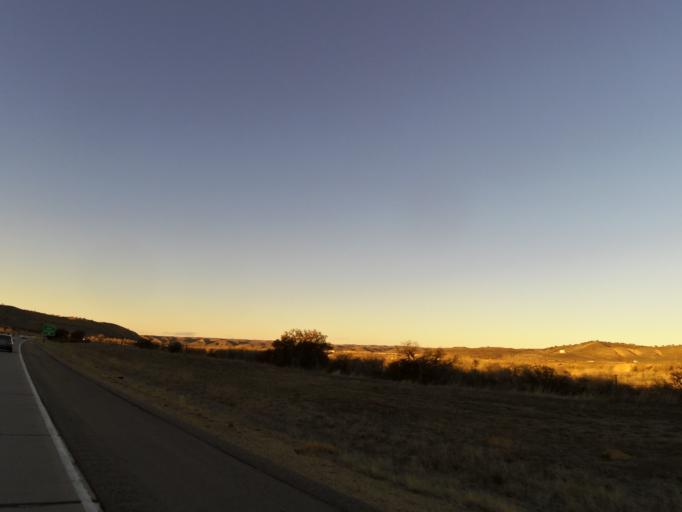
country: US
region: California
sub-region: San Luis Obispo County
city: San Miguel
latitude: 35.8080
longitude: -120.7502
